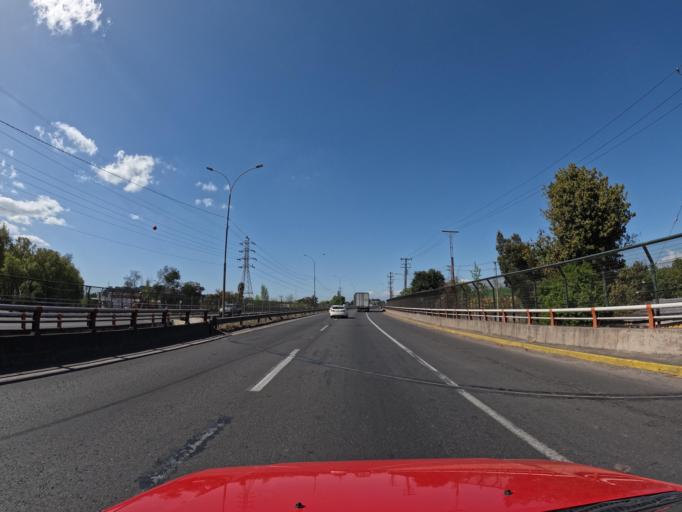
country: CL
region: Maule
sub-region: Provincia de Curico
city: Curico
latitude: -34.9948
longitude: -71.2325
